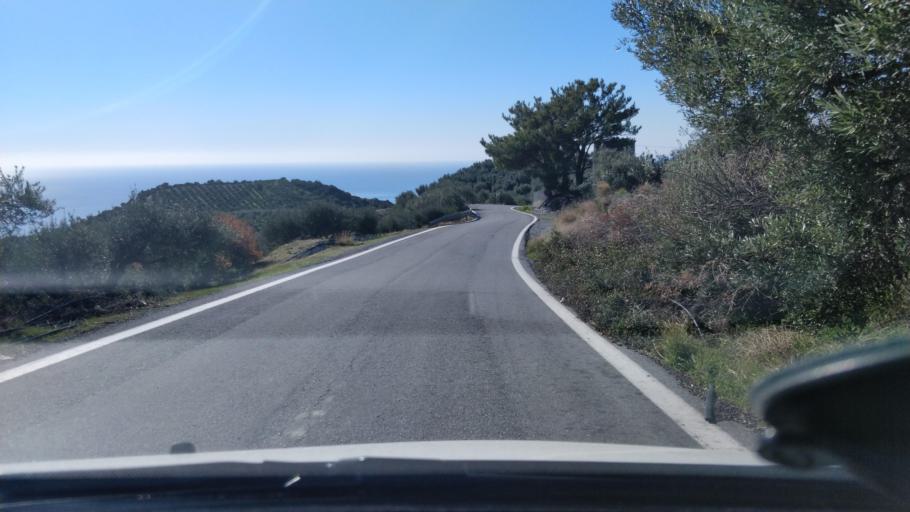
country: GR
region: Crete
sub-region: Nomos Irakleiou
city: Arkalochori
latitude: 35.0100
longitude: 25.4432
